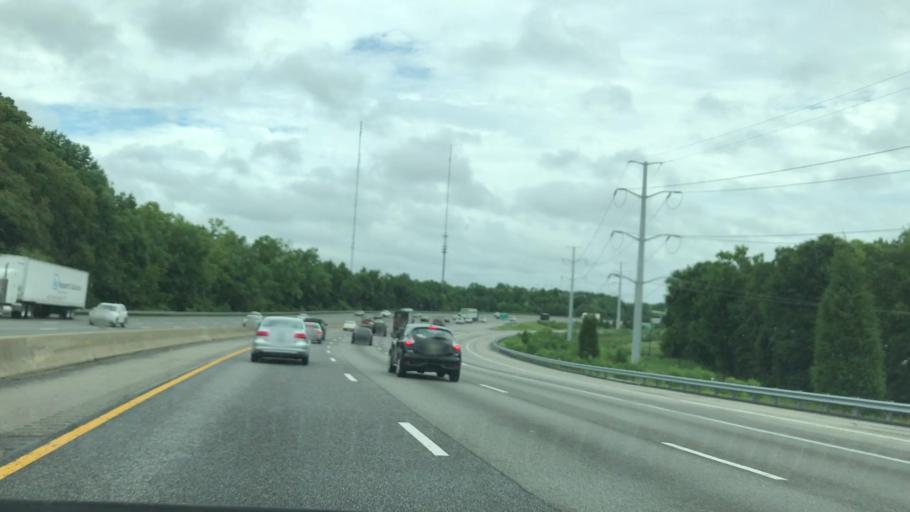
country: US
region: Virginia
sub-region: Chesterfield County
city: Bellwood
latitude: 37.4317
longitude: -77.4313
